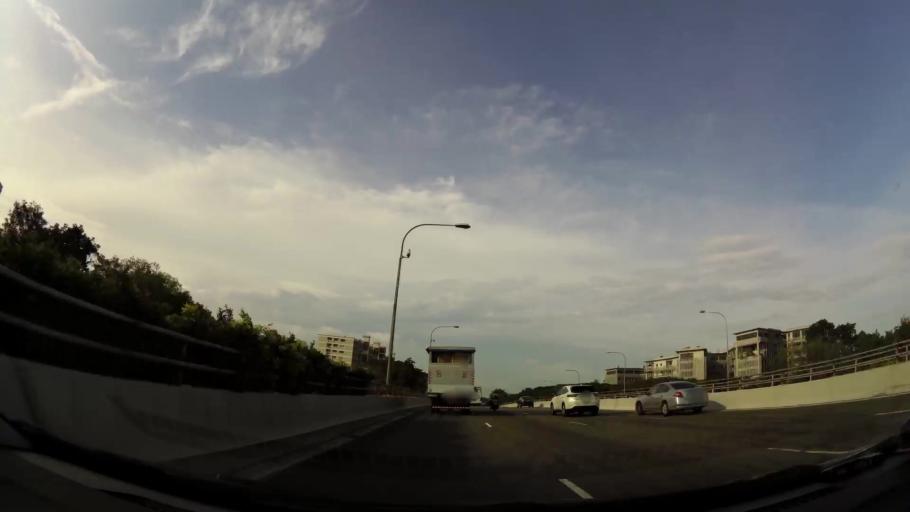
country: MY
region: Johor
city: Johor Bahru
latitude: 1.3463
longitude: 103.6910
